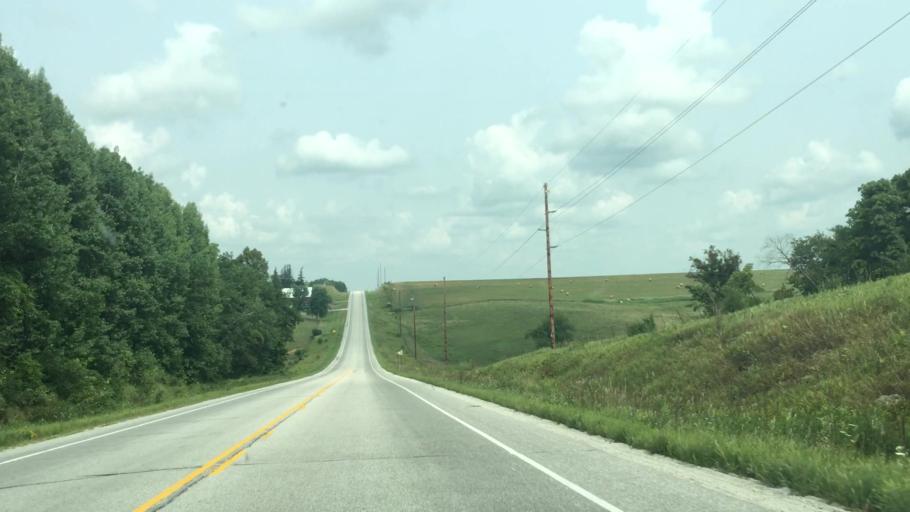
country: US
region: Minnesota
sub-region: Fillmore County
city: Harmony
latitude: 43.5730
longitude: -91.9298
